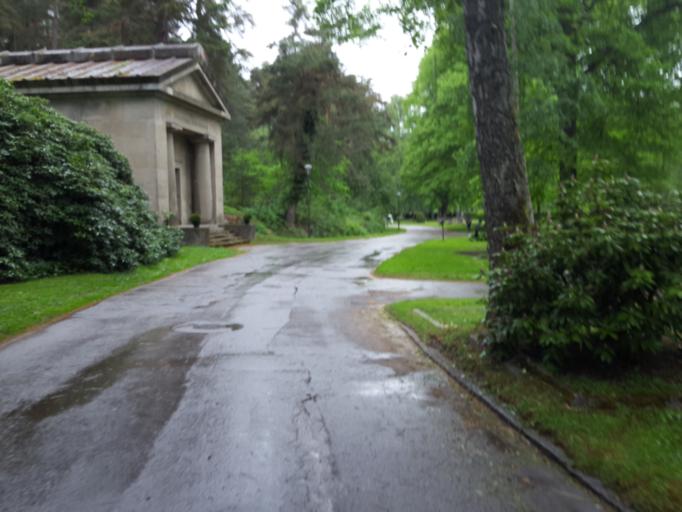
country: SE
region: Stockholm
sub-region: Solna Kommun
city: Solna
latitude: 59.3577
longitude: 18.0247
